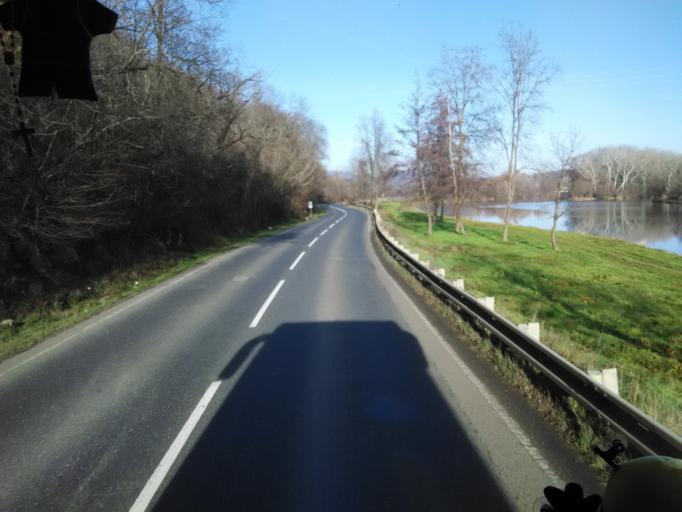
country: SK
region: Nitriansky
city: Tlmace
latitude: 48.2938
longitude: 18.5283
